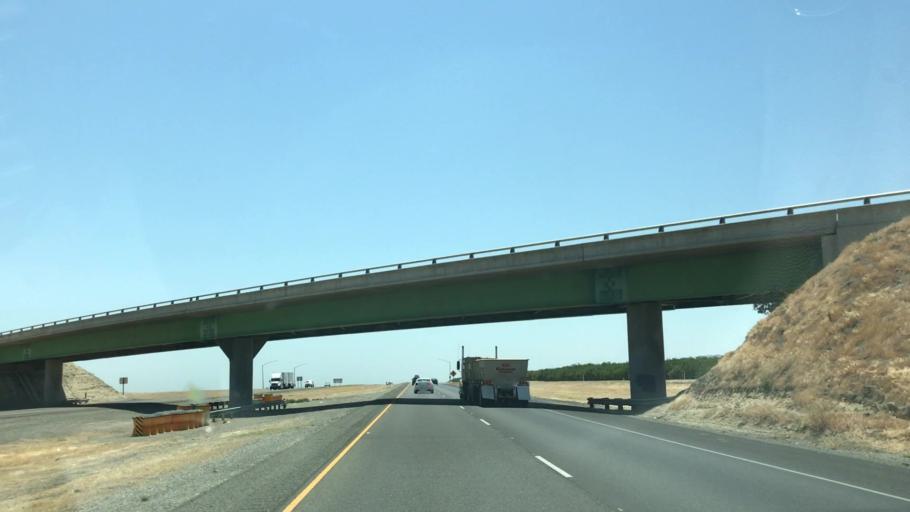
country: US
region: California
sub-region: Fresno County
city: Mendota
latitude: 36.6038
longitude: -120.5859
